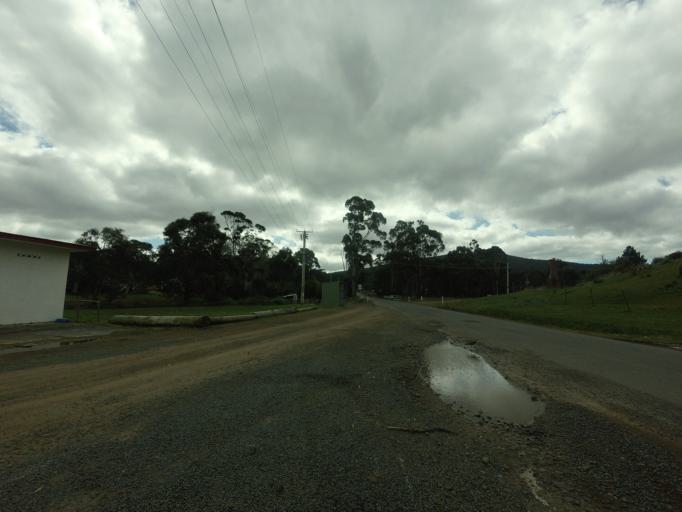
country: AU
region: Tasmania
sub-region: Huon Valley
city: Geeveston
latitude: -43.4315
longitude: 146.9742
